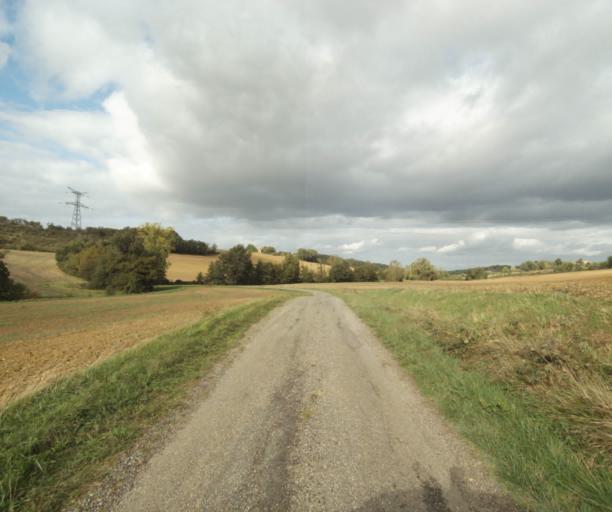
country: FR
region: Midi-Pyrenees
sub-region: Departement du Tarn-et-Garonne
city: Beaumont-de-Lomagne
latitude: 43.9102
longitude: 1.0950
